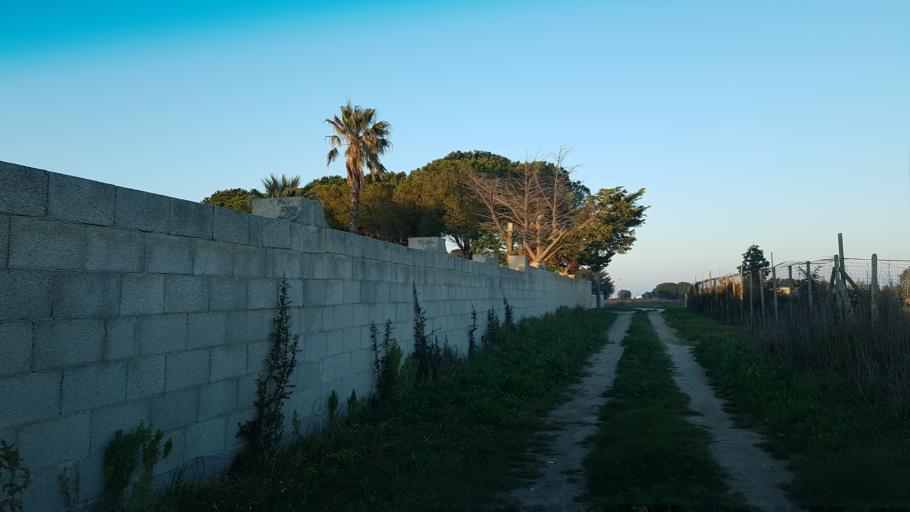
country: IT
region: Apulia
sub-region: Provincia di Brindisi
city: Brindisi
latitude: 40.6519
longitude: 17.9278
